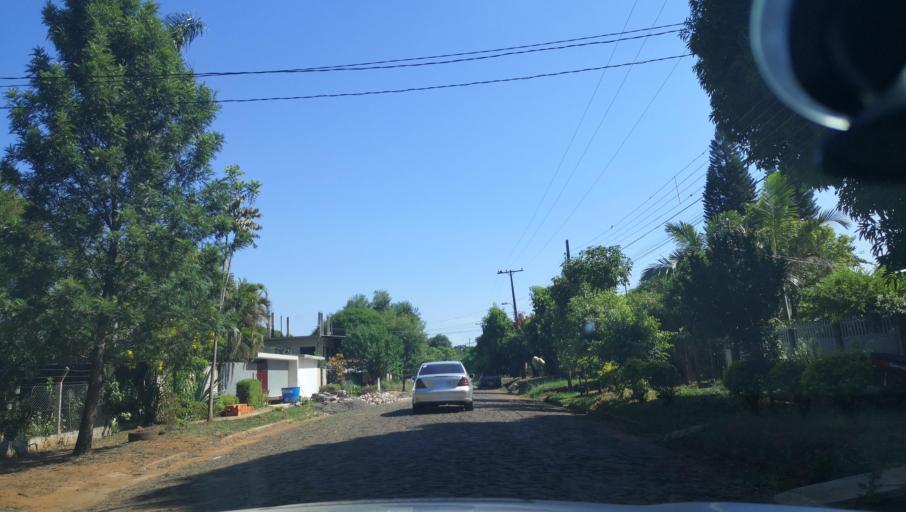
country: PY
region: Itapua
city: Carmen del Parana
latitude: -27.1572
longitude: -56.2333
